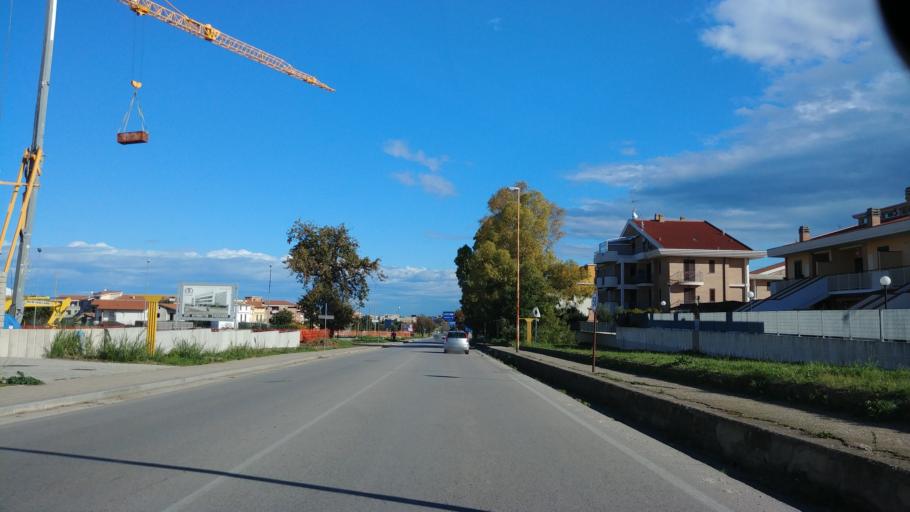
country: IT
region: Molise
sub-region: Provincia di Campobasso
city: Termoli
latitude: 41.9912
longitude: 14.9751
